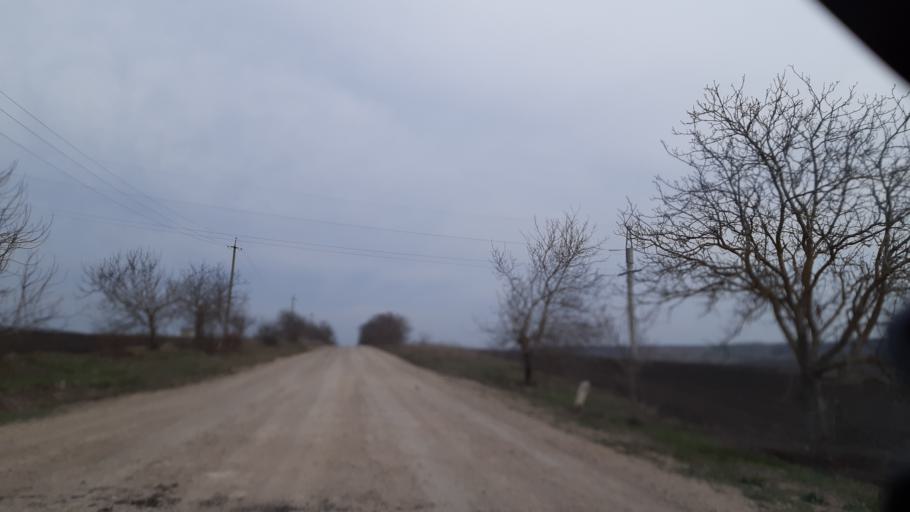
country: MD
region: Soldanesti
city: Soldanesti
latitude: 47.7022
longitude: 28.7200
